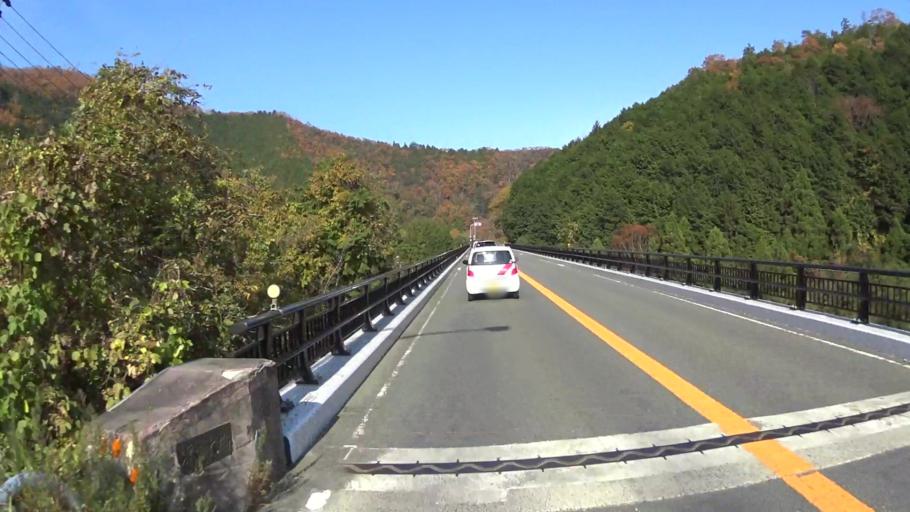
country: JP
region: Kyoto
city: Ayabe
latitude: 35.2000
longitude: 135.2821
